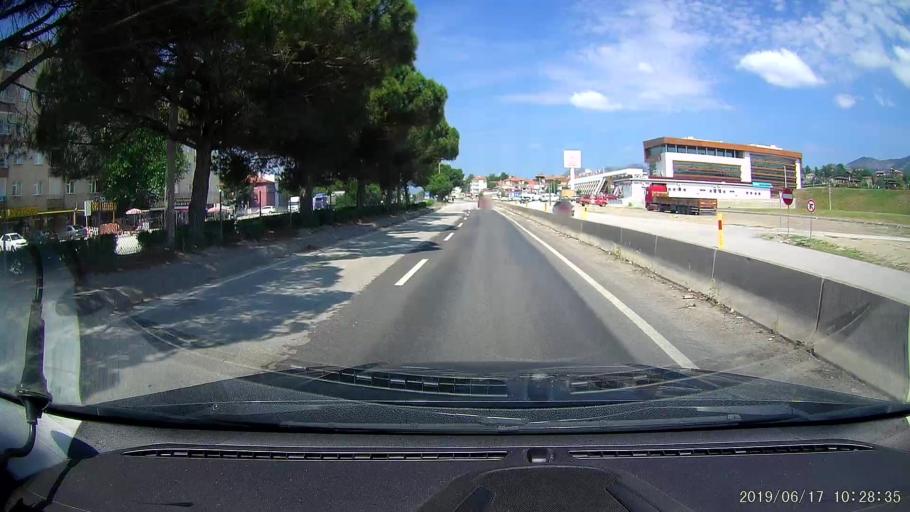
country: TR
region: Corum
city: Osmancik
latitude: 40.9788
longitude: 34.8059
